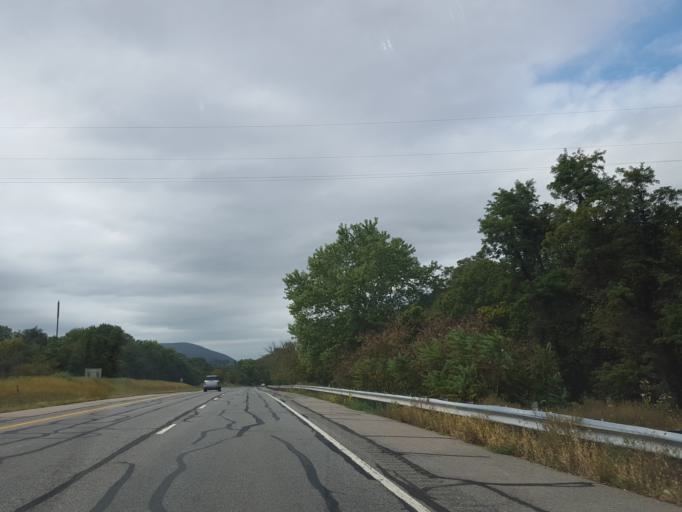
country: US
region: Maryland
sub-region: Frederick County
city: Brunswick
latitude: 39.3316
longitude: -77.6615
